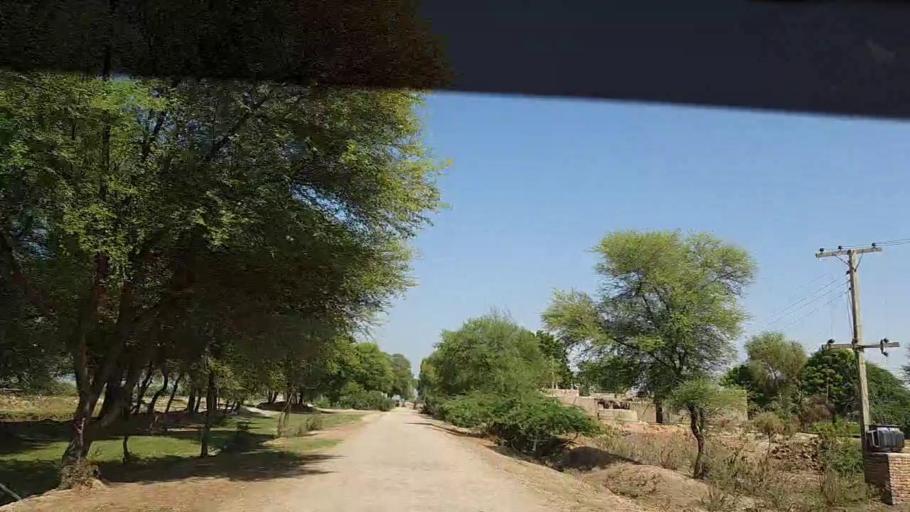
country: PK
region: Sindh
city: Tangwani
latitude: 28.2914
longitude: 69.0841
